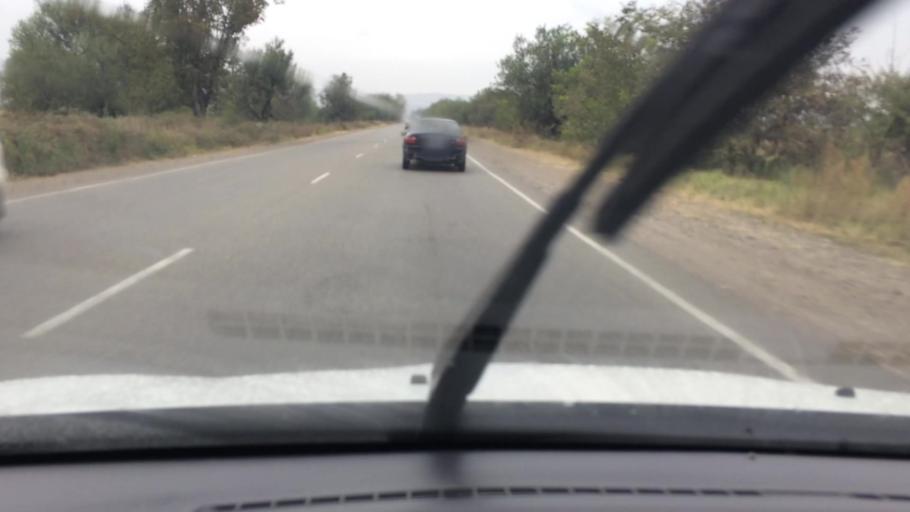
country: GE
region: Kvemo Kartli
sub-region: Marneuli
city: Marneuli
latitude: 41.5620
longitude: 44.7758
